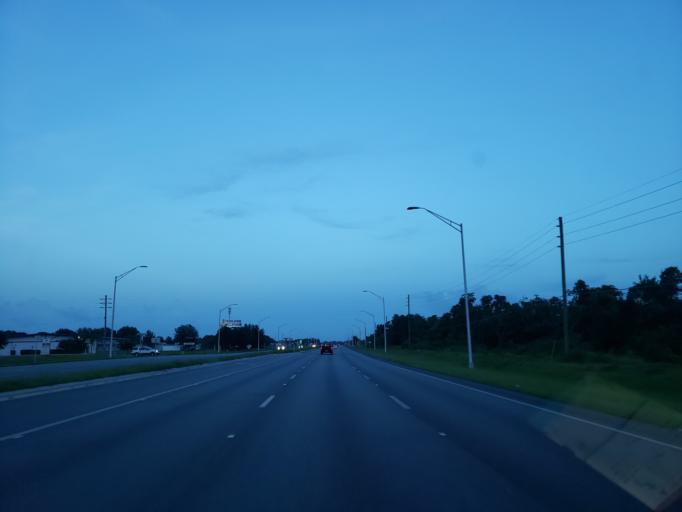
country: US
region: Florida
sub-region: Osceola County
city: Saint Cloud
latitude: 28.2456
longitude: -81.2327
